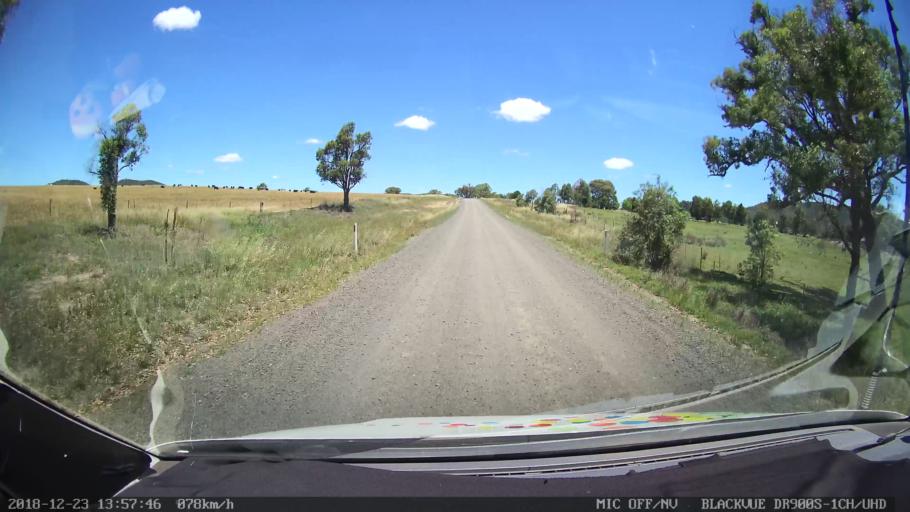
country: AU
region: New South Wales
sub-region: Tamworth Municipality
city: Manilla
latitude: -30.5917
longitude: 151.0933
